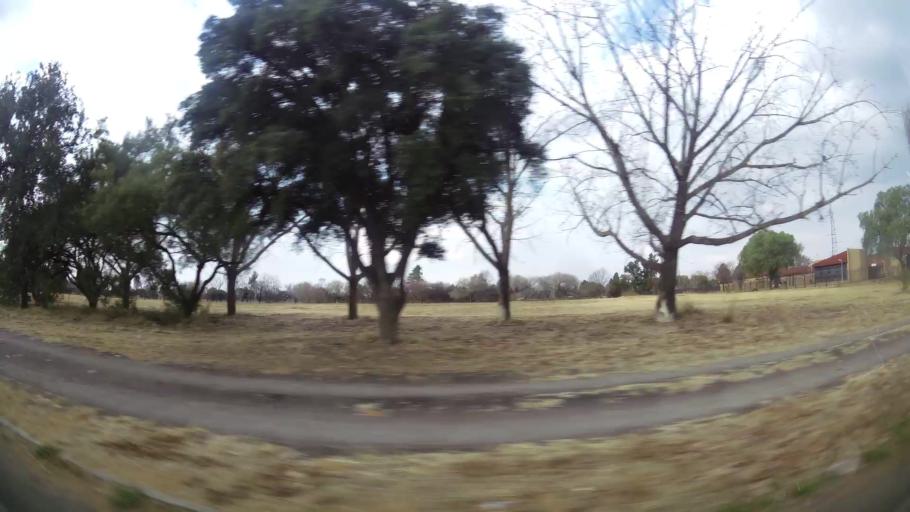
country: ZA
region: Orange Free State
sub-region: Fezile Dabi District Municipality
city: Sasolburg
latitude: -26.8009
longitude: 27.8294
